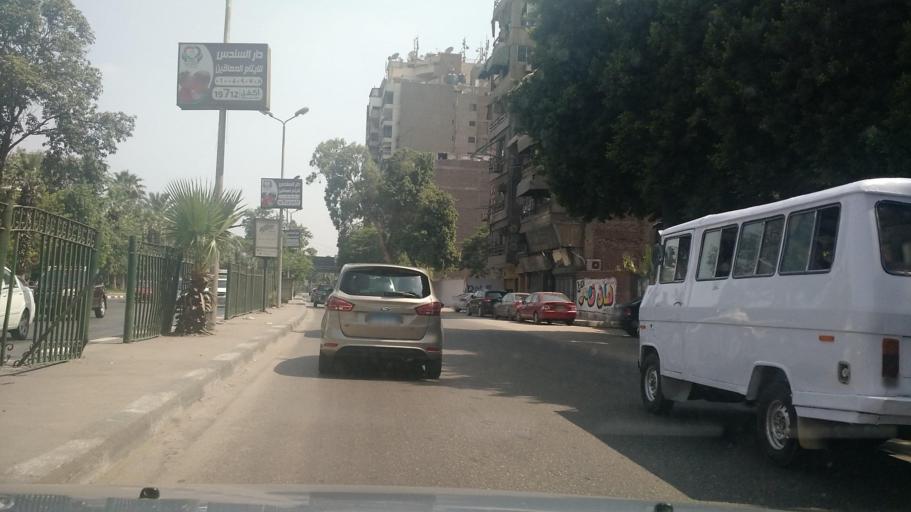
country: EG
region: Al Jizah
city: Al Jizah
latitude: 30.0069
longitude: 31.2266
